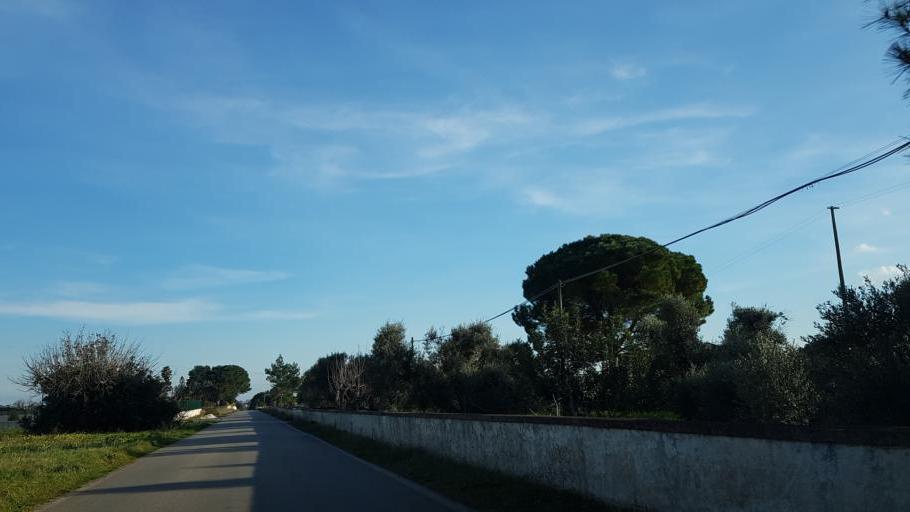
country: IT
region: Apulia
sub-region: Provincia di Brindisi
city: San Vito dei Normanni
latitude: 40.6835
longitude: 17.7680
